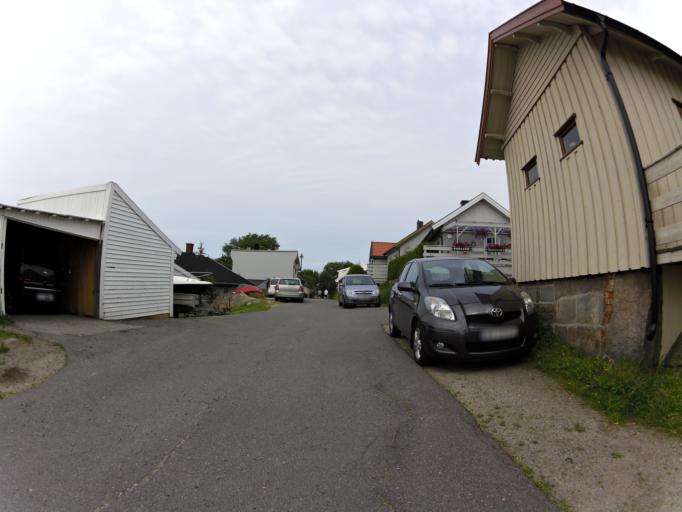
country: NO
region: Ostfold
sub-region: Fredrikstad
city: Fredrikstad
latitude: 59.2145
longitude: 10.9679
